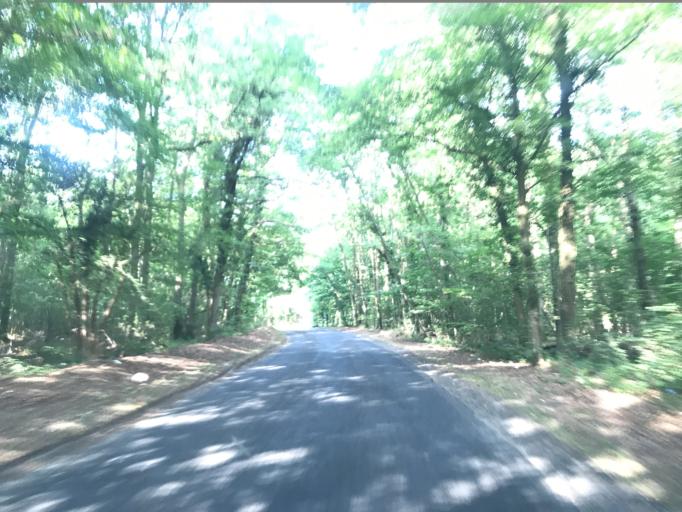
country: FR
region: Ile-de-France
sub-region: Departement des Yvelines
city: Freneuse
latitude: 49.0610
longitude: 1.5853
